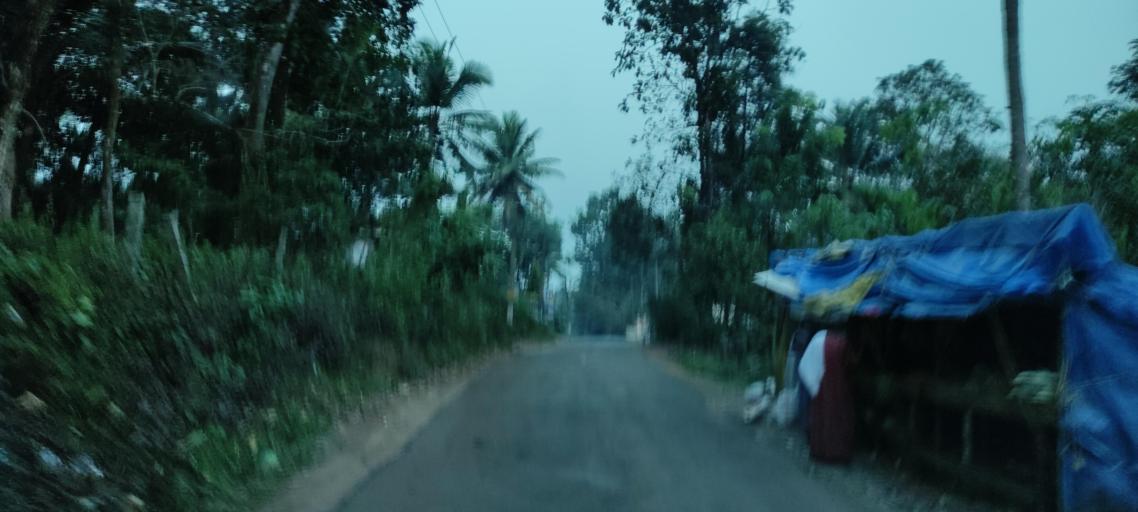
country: IN
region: Kerala
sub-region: Pattanamtitta
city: Adur
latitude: 9.1592
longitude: 76.7545
